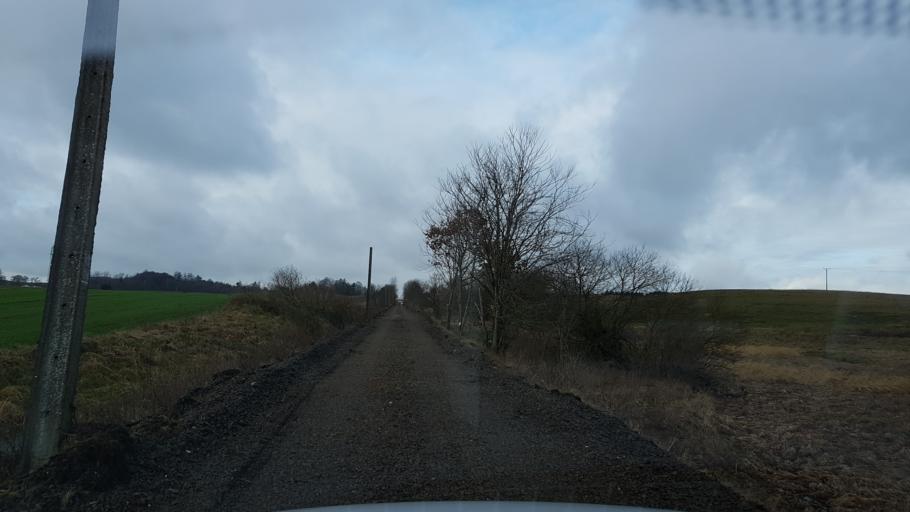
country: PL
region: West Pomeranian Voivodeship
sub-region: Powiat swidwinski
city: Polczyn-Zdroj
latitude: 53.7837
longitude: 16.0604
